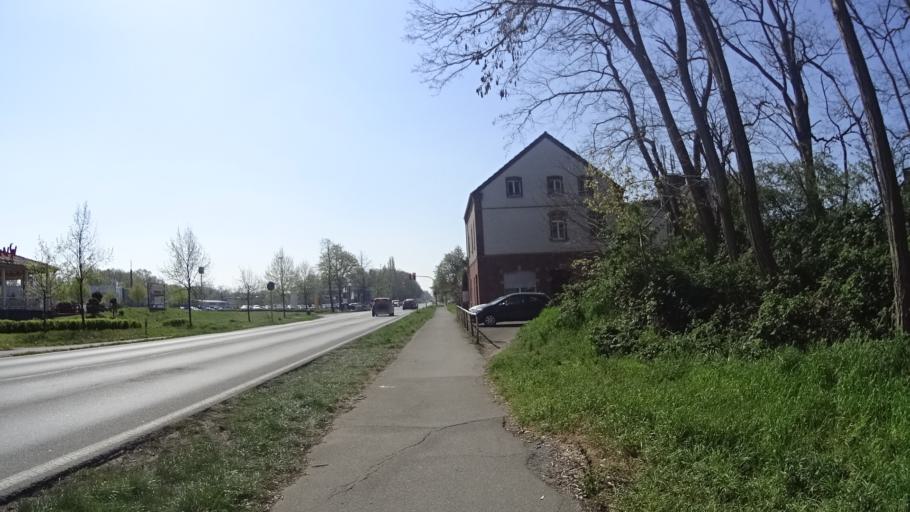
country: DE
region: North Rhine-Westphalia
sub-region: Regierungsbezirk Dusseldorf
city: Moers
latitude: 51.4764
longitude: 6.6320
